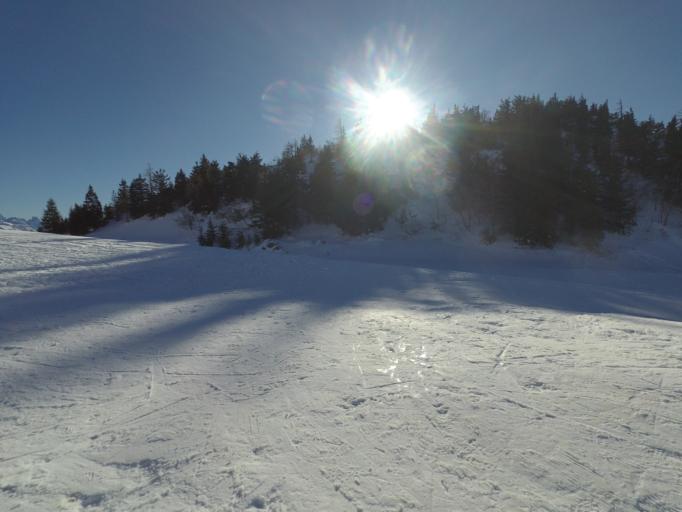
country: AT
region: Salzburg
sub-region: Politischer Bezirk Hallein
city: Scheffau am Tennengebirge
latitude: 47.6358
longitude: 13.2609
